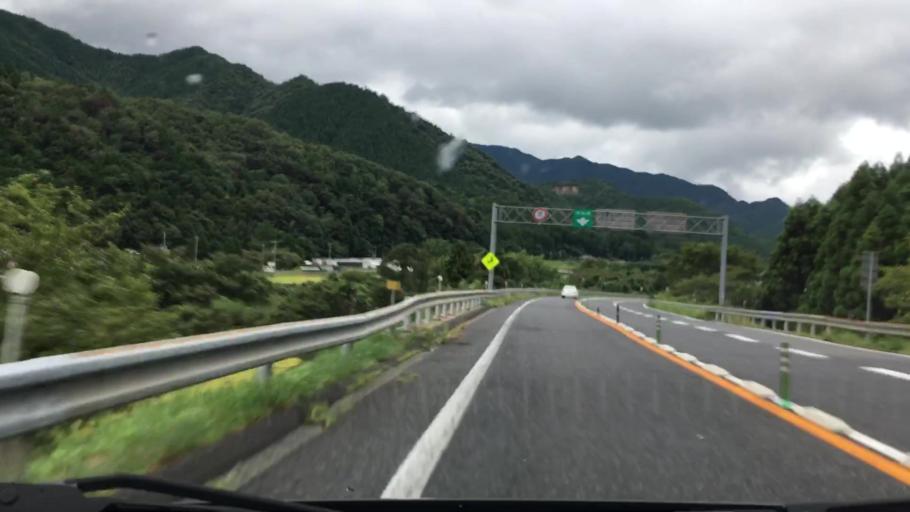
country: JP
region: Hyogo
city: Nishiwaki
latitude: 35.0924
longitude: 134.7765
